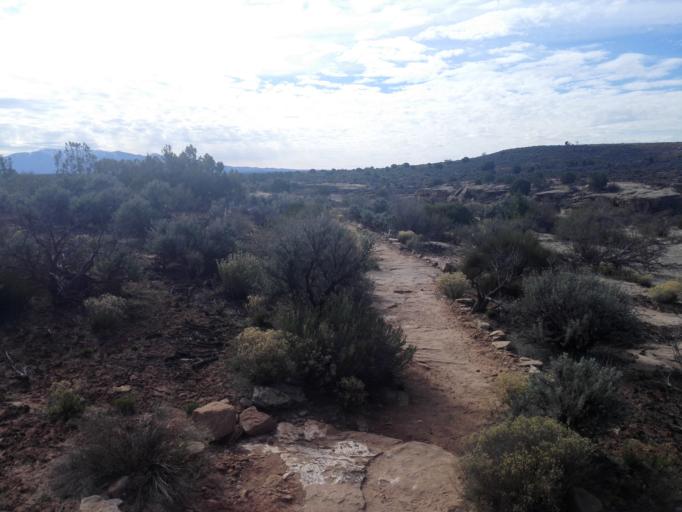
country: US
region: Colorado
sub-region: Montezuma County
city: Towaoc
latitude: 37.3855
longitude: -109.0799
